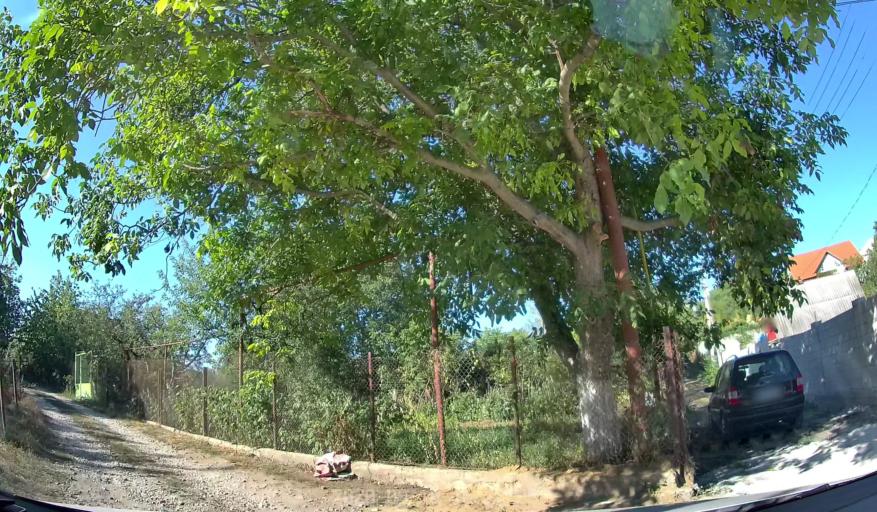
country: MD
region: Chisinau
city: Stauceni
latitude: 47.0571
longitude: 28.9227
